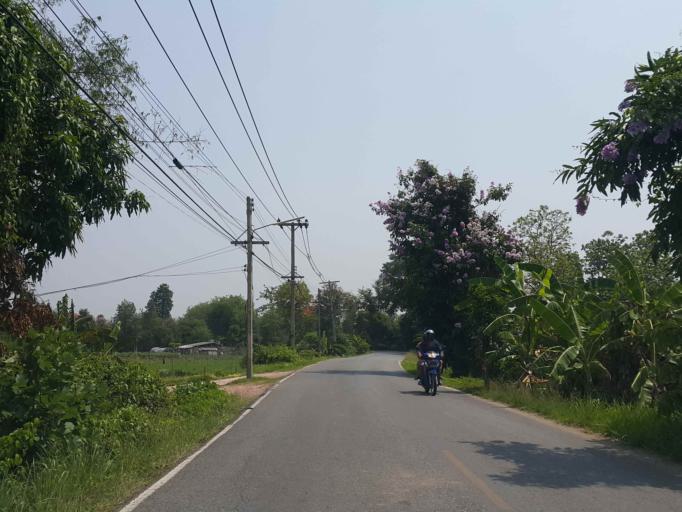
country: TH
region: Chiang Mai
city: San Sai
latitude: 18.8787
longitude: 98.9796
